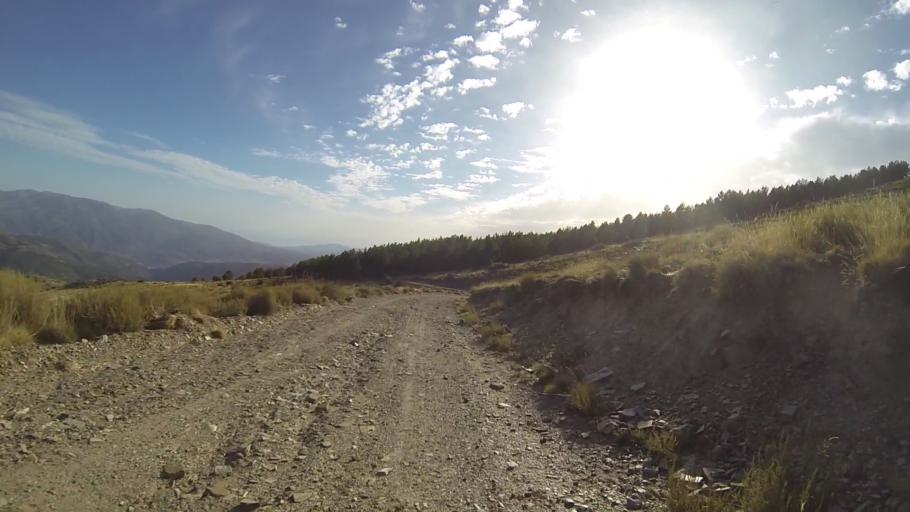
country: ES
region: Andalusia
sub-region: Provincia de Almeria
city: Laujar de Andarax
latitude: 37.0726
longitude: -2.8895
